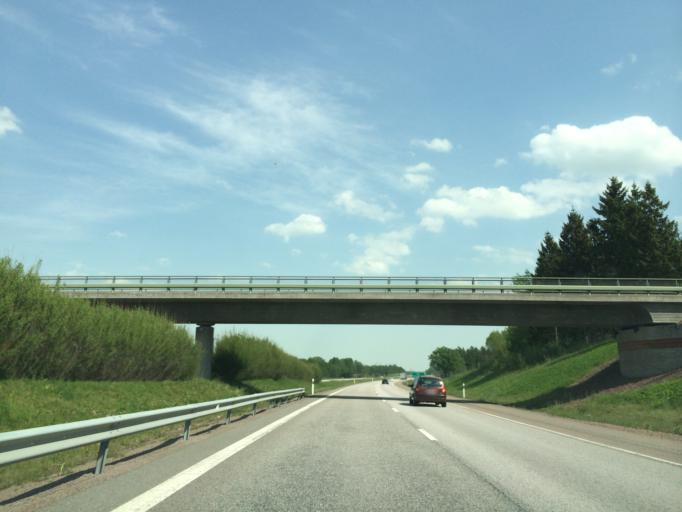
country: SE
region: OEstergoetland
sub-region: Boxholms Kommun
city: Boxholm
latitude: 58.3005
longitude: 14.9442
